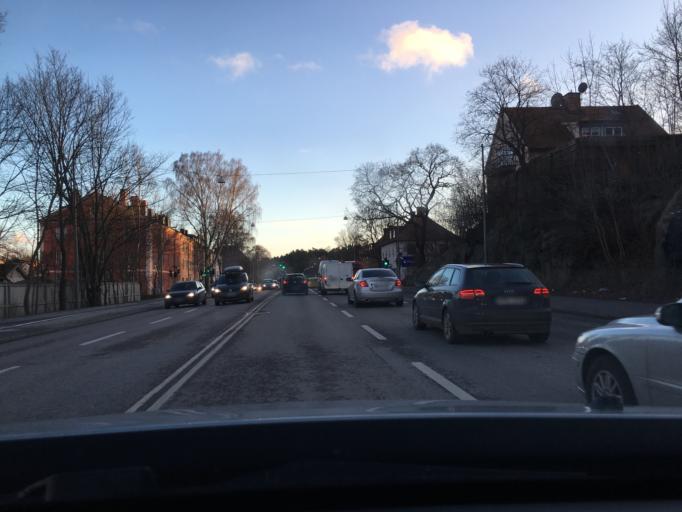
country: SE
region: Stockholm
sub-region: Sundbybergs Kommun
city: Sundbyberg
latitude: 59.3385
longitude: 17.9644
